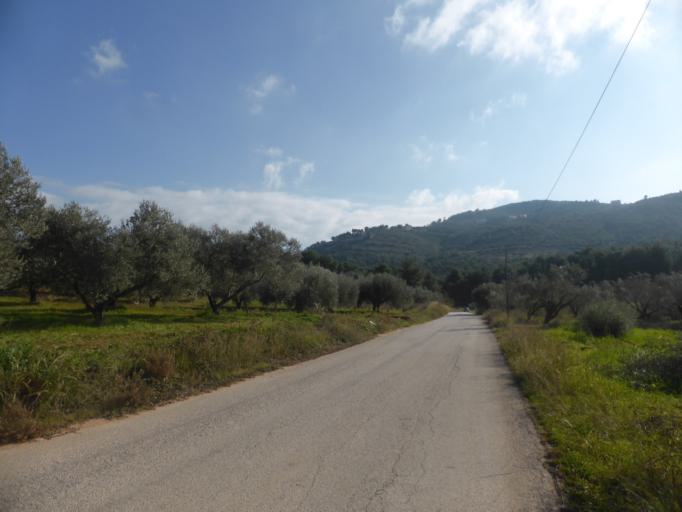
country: GR
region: Attica
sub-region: Nomarchia Anatolikis Attikis
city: Markopoulo Oropou
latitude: 38.2947
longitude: 23.8445
